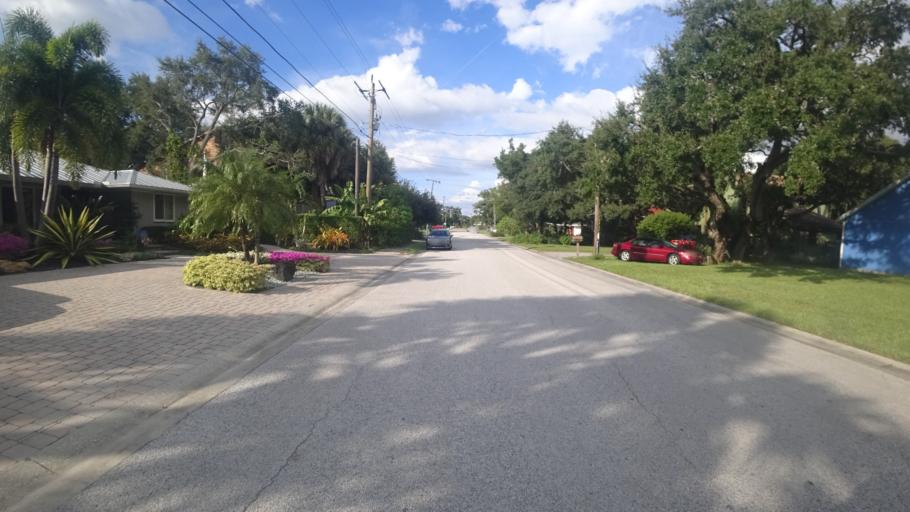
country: US
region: Florida
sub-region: Manatee County
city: Palmetto
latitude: 27.5203
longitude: -82.5893
